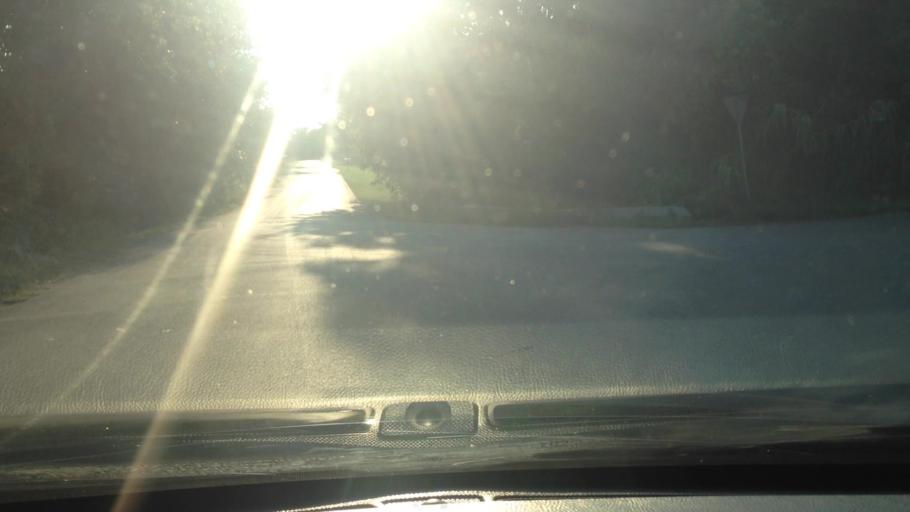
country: US
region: Texas
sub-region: Tarrant County
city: Rendon
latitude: 32.5838
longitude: -97.2497
